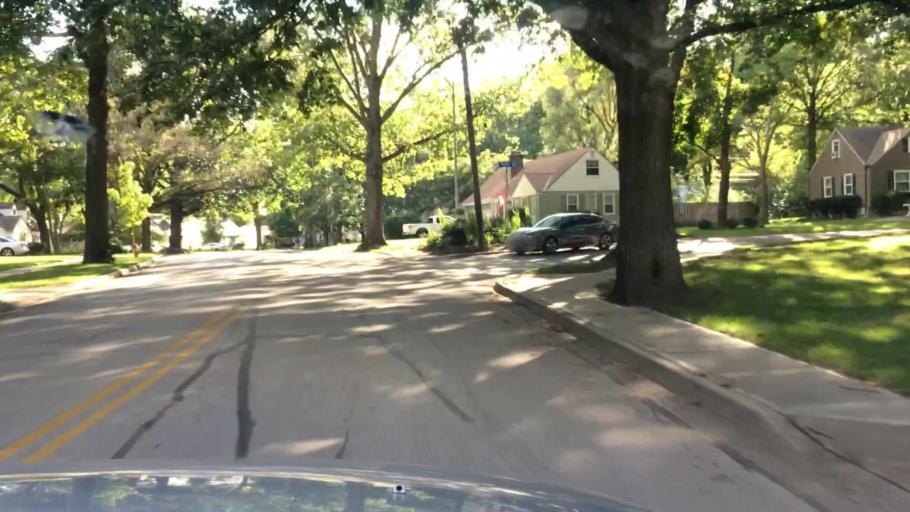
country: US
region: Kansas
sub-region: Johnson County
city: Prairie Village
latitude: 38.9965
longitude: -94.6409
